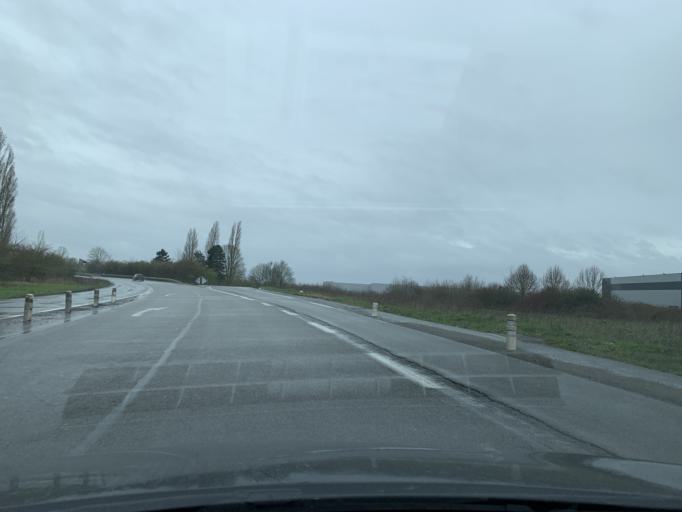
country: FR
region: Nord-Pas-de-Calais
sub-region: Departement du Nord
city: Herin
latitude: 50.3413
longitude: 3.4653
